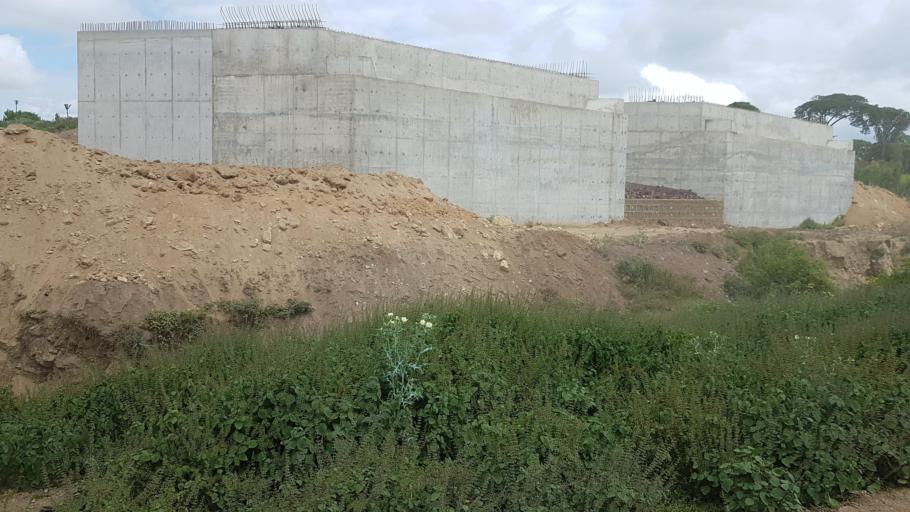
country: ET
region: Oromiya
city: Shashemene
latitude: 7.2489
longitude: 38.5899
